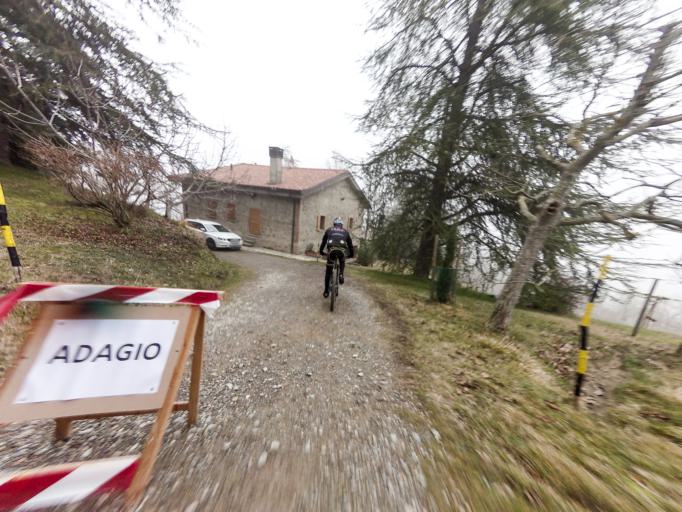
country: IT
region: Emilia-Romagna
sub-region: Provincia di Bologna
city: Pianoro
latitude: 44.3379
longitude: 11.3238
